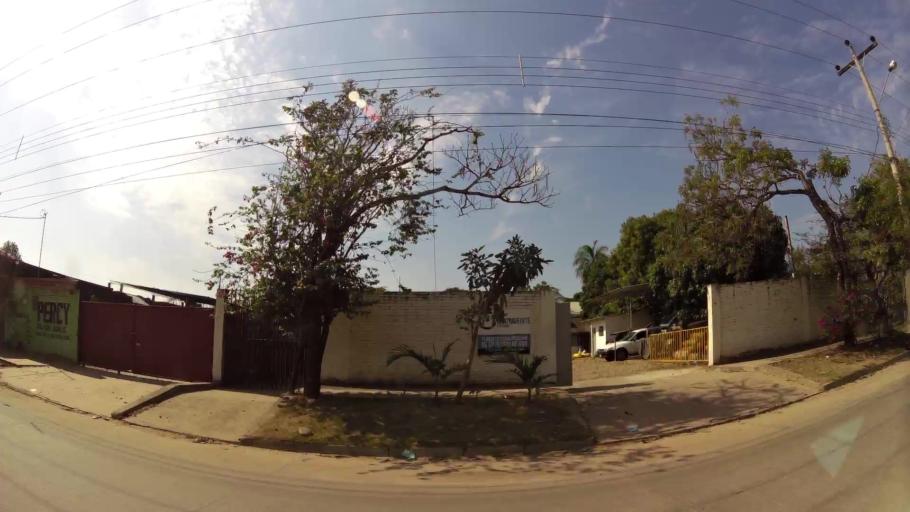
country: BO
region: Santa Cruz
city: Santa Cruz de la Sierra
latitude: -17.7256
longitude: -63.1574
